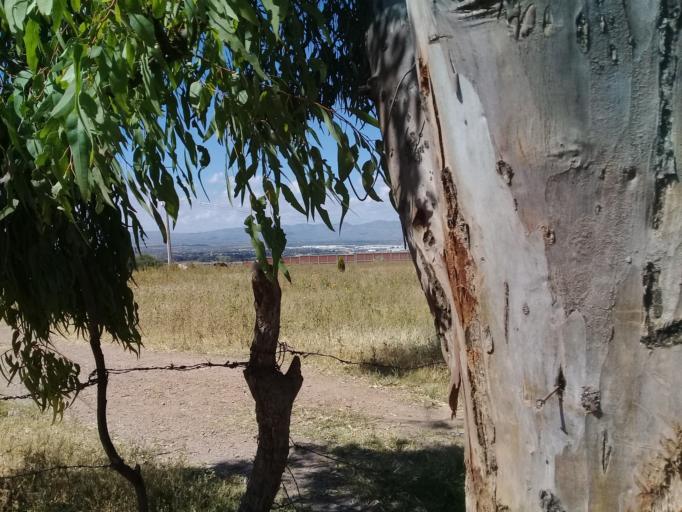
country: MX
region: Aguascalientes
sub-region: Aguascalientes
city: San Sebastian [Fraccionamiento]
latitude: 21.7820
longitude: -102.2505
